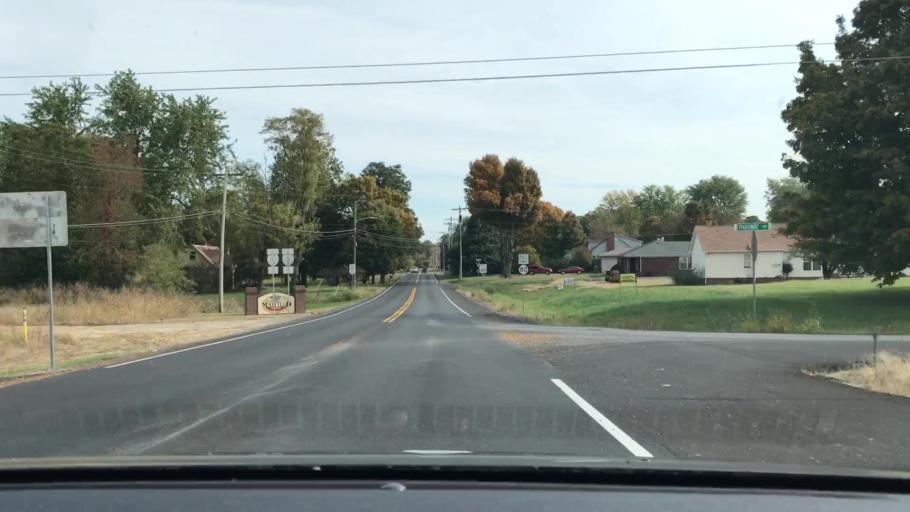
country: US
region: Kentucky
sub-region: Graves County
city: Mayfield
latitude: 36.7398
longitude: -88.6657
